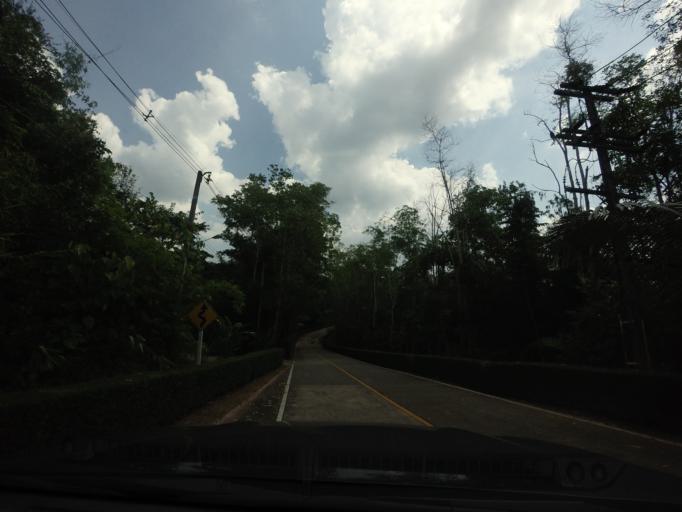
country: TH
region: Nan
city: Bo Kluea
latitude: 19.0230
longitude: 101.2068
